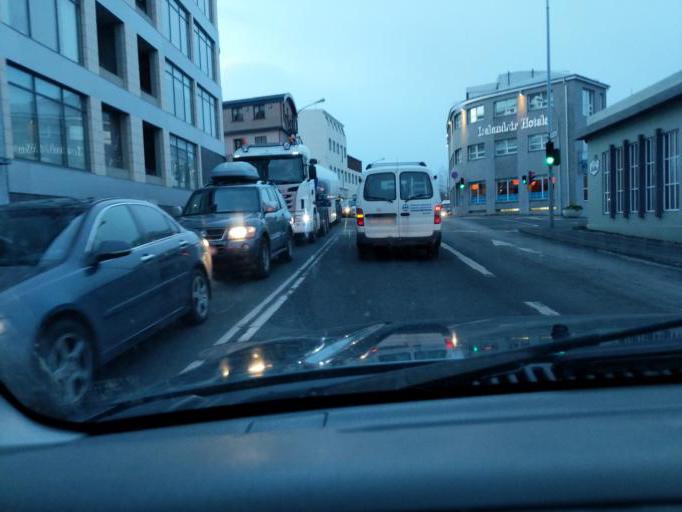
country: IS
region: Capital Region
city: Kopavogur
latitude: 64.1508
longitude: -21.9447
